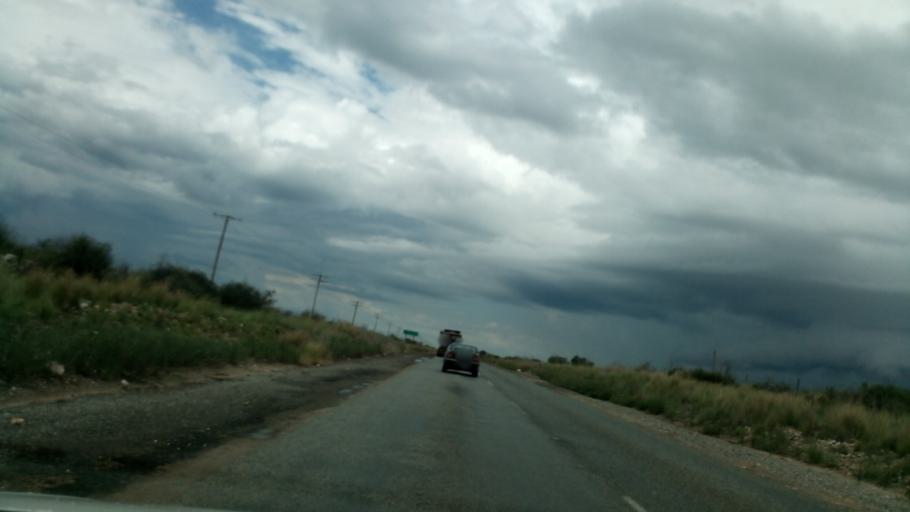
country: ZA
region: Northern Cape
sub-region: Frances Baard District Municipality
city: Barkly West
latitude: -28.2659
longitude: 24.0671
